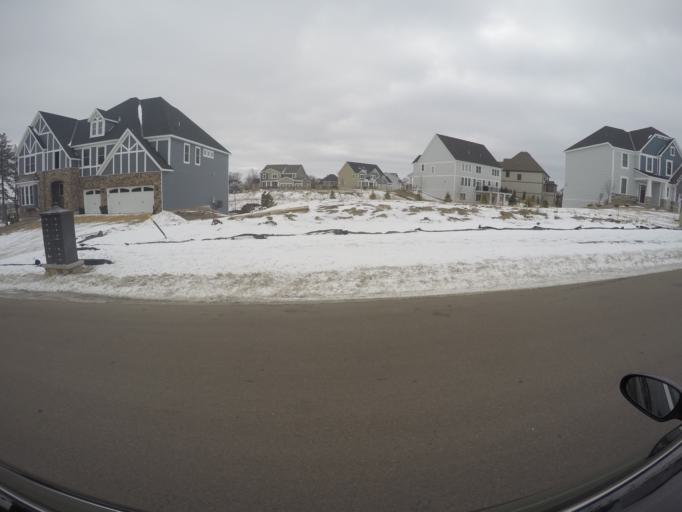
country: US
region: Minnesota
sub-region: Hennepin County
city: Eden Prairie
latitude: 44.8242
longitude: -93.4868
